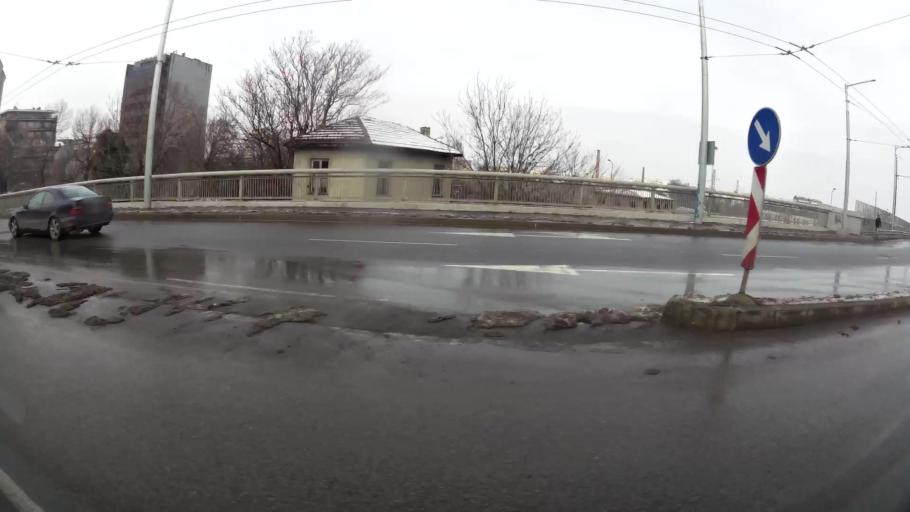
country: BG
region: Sofia-Capital
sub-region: Stolichna Obshtina
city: Sofia
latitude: 42.6996
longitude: 23.3440
